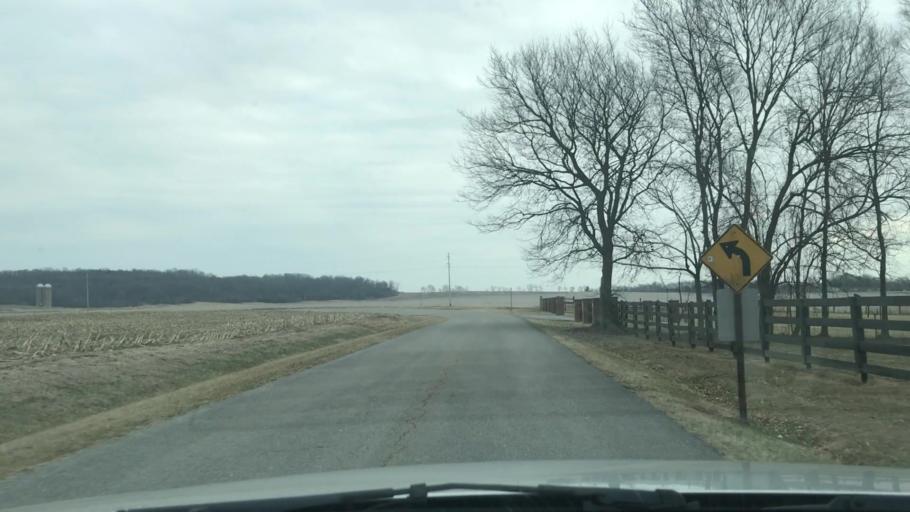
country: US
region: Kentucky
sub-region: Edmonson County
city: Brownsville
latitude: 37.0490
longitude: -86.2420
